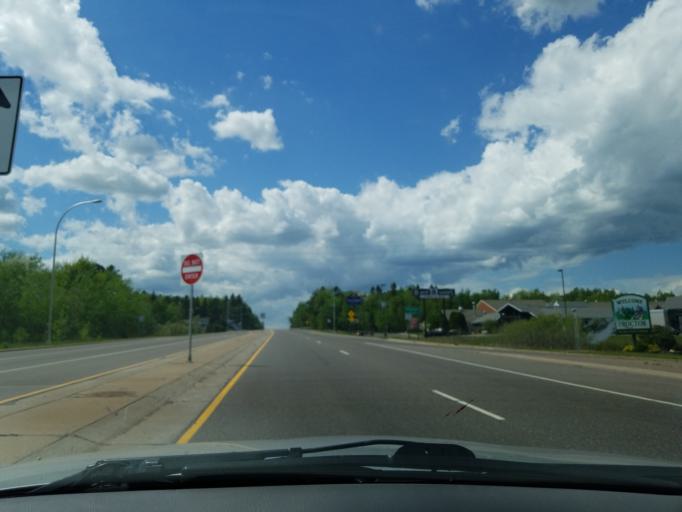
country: US
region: Minnesota
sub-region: Saint Louis County
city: Proctor
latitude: 46.7383
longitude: -92.2173
